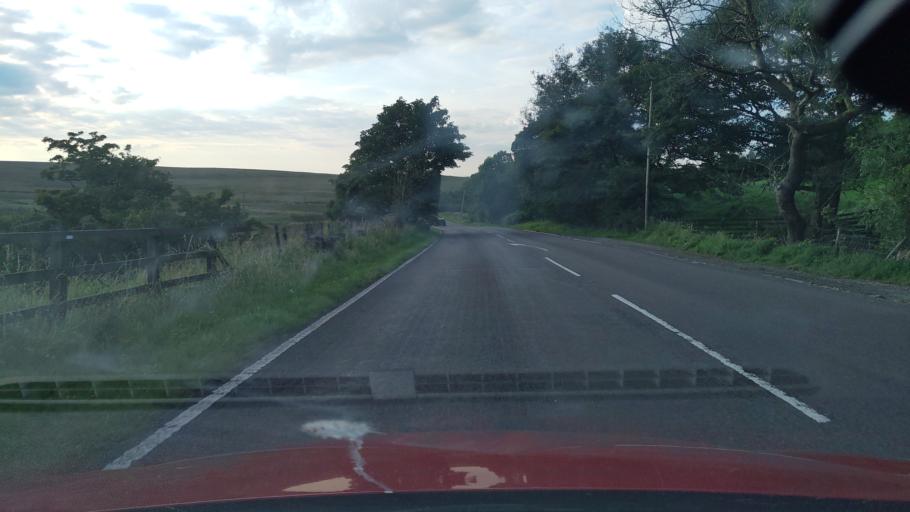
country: GB
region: England
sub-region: Blackburn with Darwen
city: Darwen
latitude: 53.6734
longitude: -2.5159
